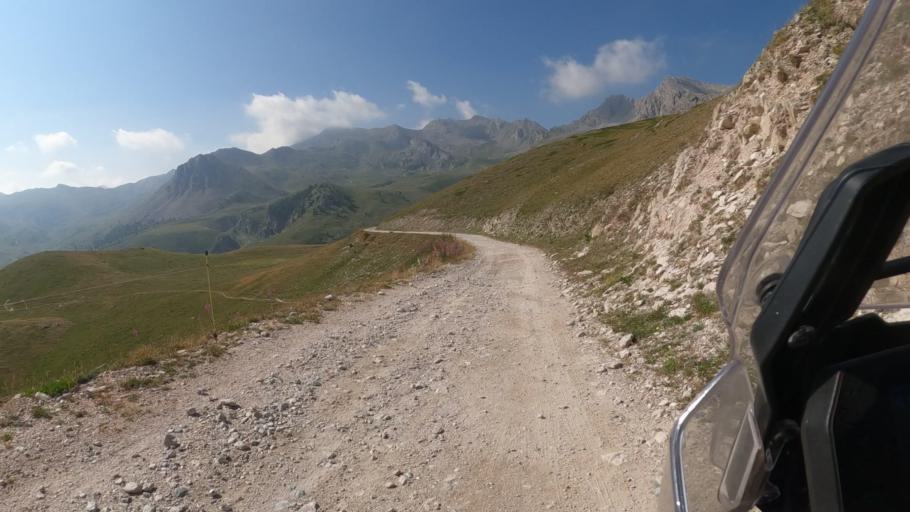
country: IT
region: Piedmont
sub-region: Provincia di Cuneo
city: Pietraporzio
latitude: 44.4057
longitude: 7.0301
